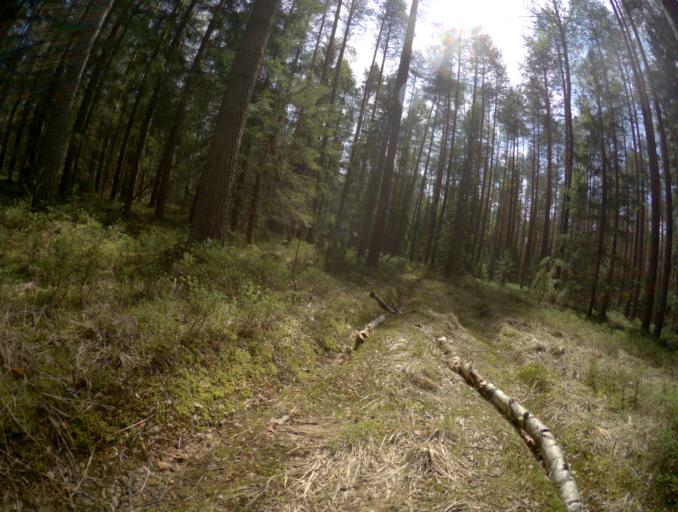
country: RU
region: Vladimir
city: Golovino
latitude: 55.9266
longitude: 40.3662
